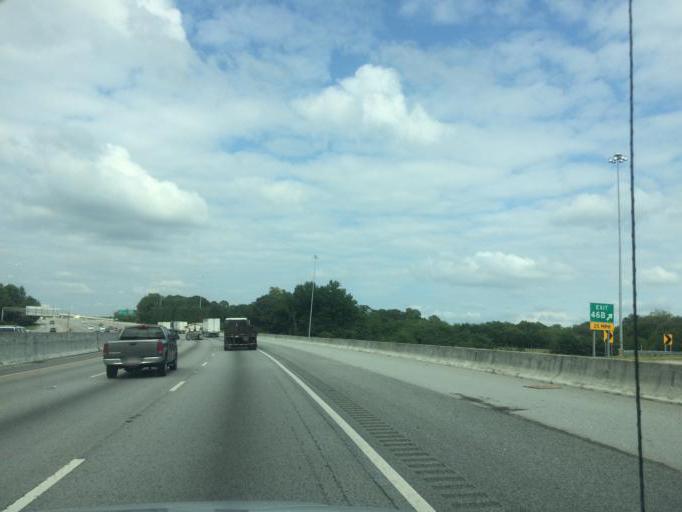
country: US
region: South Carolina
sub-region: Greenville County
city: Gantt
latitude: 34.7967
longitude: -82.3763
